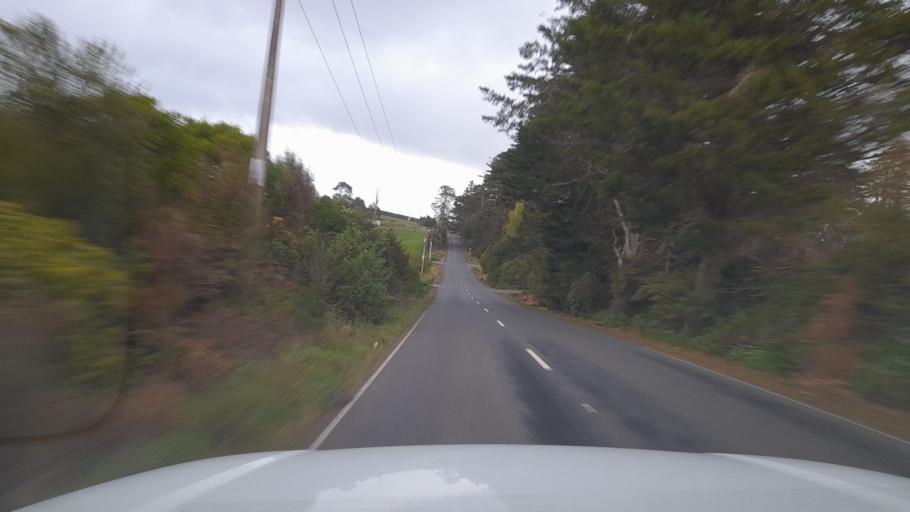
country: NZ
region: Northland
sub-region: Whangarei
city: Maungatapere
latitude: -35.7449
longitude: 174.2089
